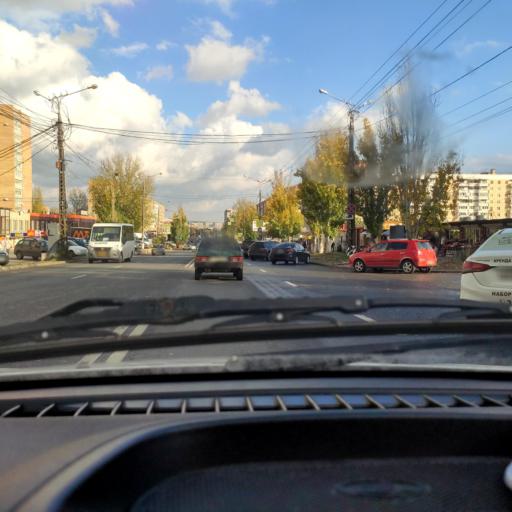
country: RU
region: Samara
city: Zhigulevsk
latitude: 53.4815
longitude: 49.4776
